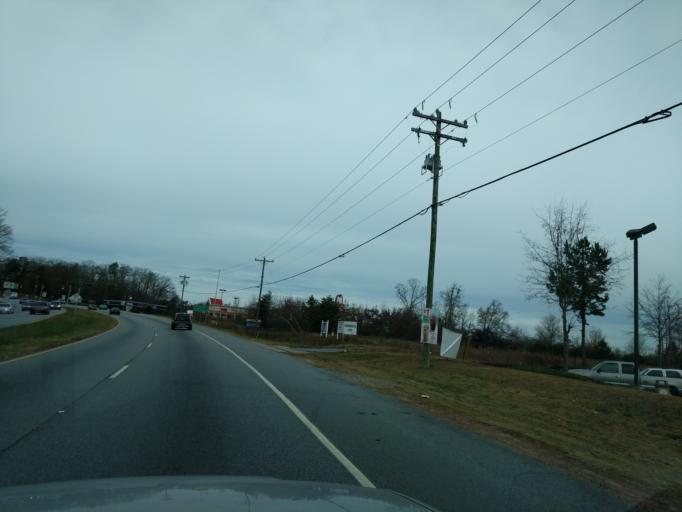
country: US
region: South Carolina
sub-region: Anderson County
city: Northlake
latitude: 34.5777
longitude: -82.7133
